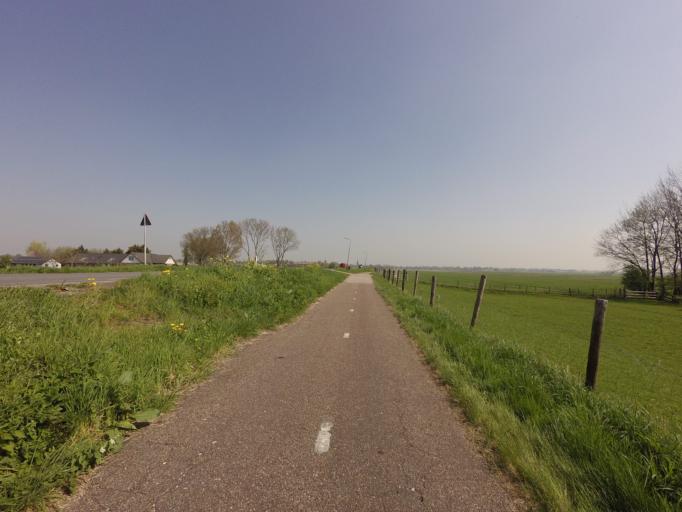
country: NL
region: Utrecht
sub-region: Gemeente De Ronde Venen
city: Mijdrecht
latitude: 52.1899
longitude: 4.8580
